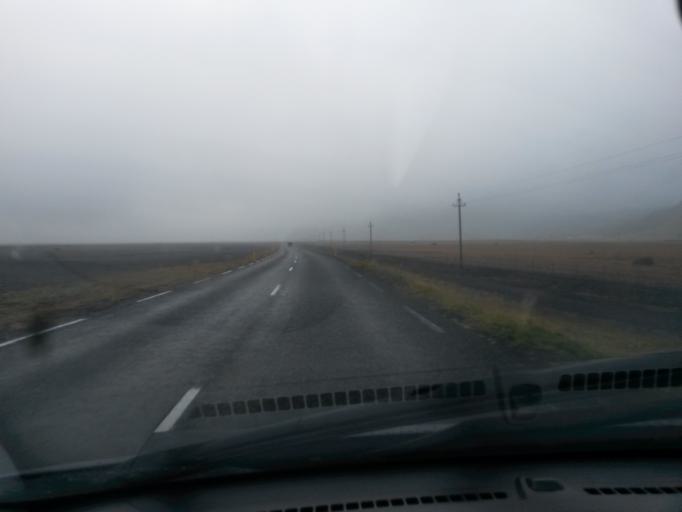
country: IS
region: South
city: Vestmannaeyjar
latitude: 63.5157
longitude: -19.4662
